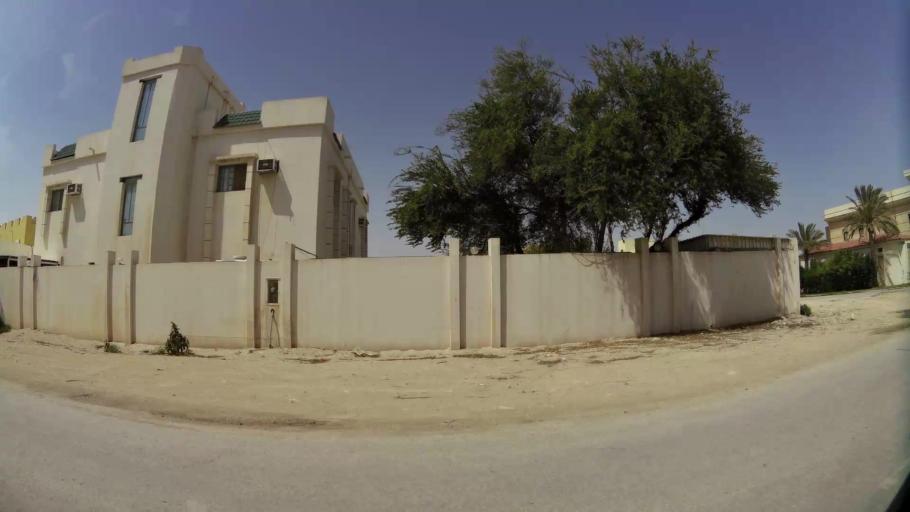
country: QA
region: Baladiyat Umm Salal
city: Umm Salal Muhammad
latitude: 25.3673
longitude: 51.4321
